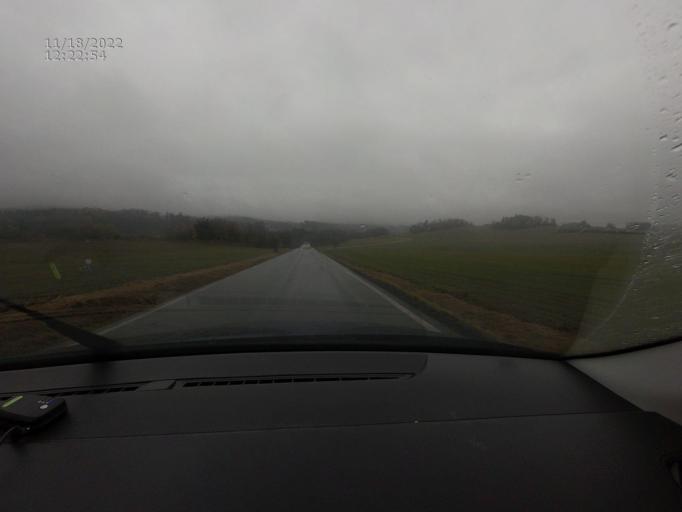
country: CZ
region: Plzensky
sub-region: Okres Plzen-Jih
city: Nepomuk
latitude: 49.4521
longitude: 13.5389
